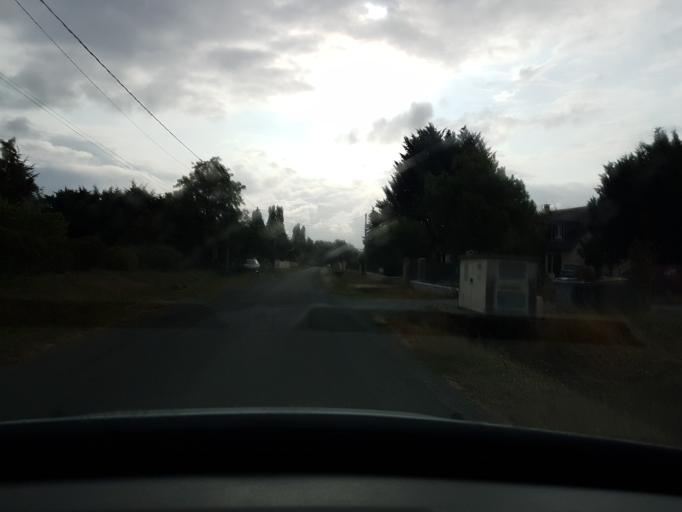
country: FR
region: Centre
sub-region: Departement d'Indre-et-Loire
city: Veretz
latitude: 47.3365
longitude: 0.8057
